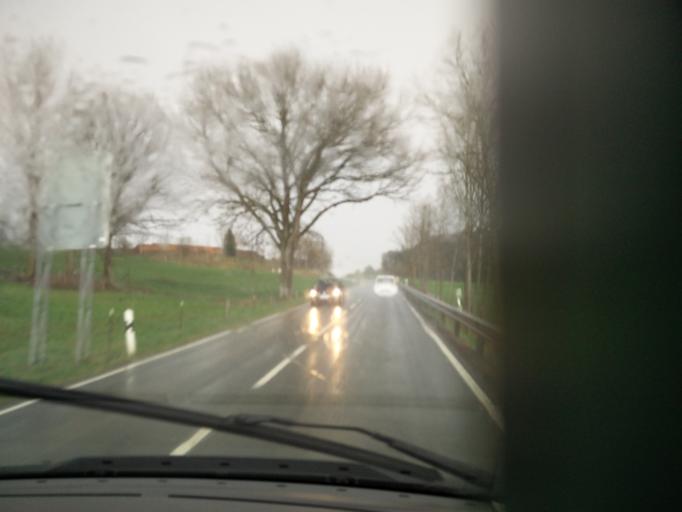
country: DE
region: Bavaria
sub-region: Upper Bavaria
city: Rimsting
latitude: 47.8883
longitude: 12.3289
